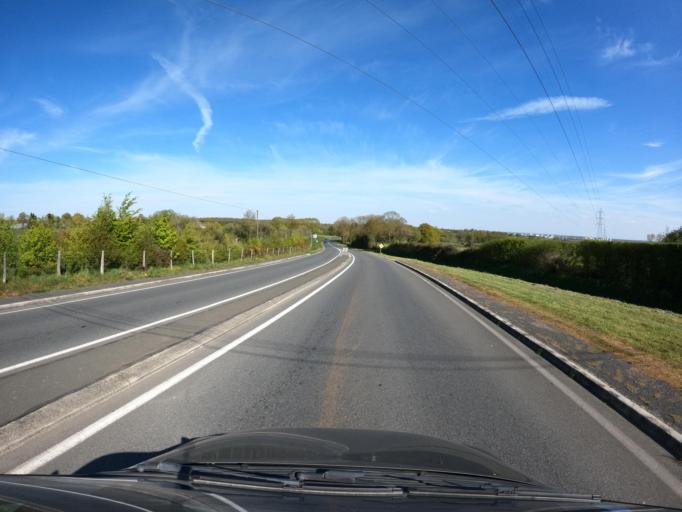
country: FR
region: Pays de la Loire
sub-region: Departement de Maine-et-Loire
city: La Seguiniere
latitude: 47.0744
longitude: -0.9331
